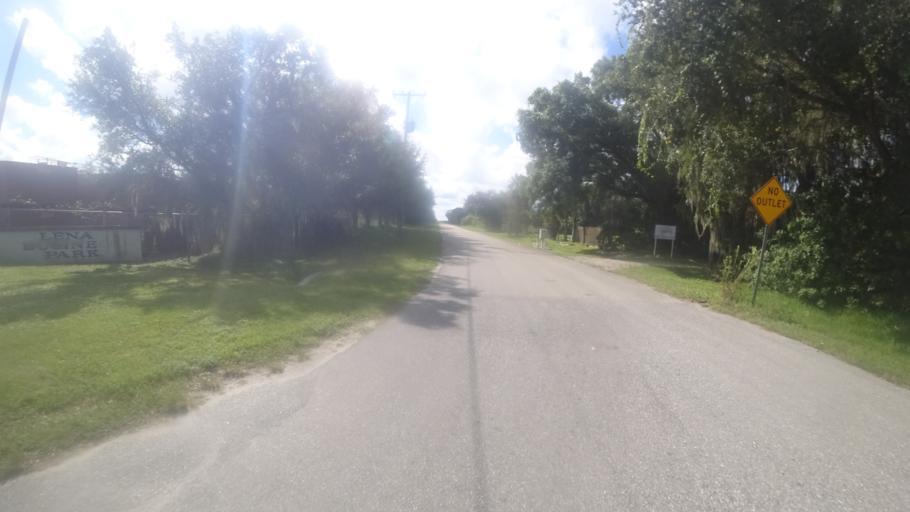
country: US
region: Florida
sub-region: Manatee County
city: Samoset
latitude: 27.4689
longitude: -82.4588
